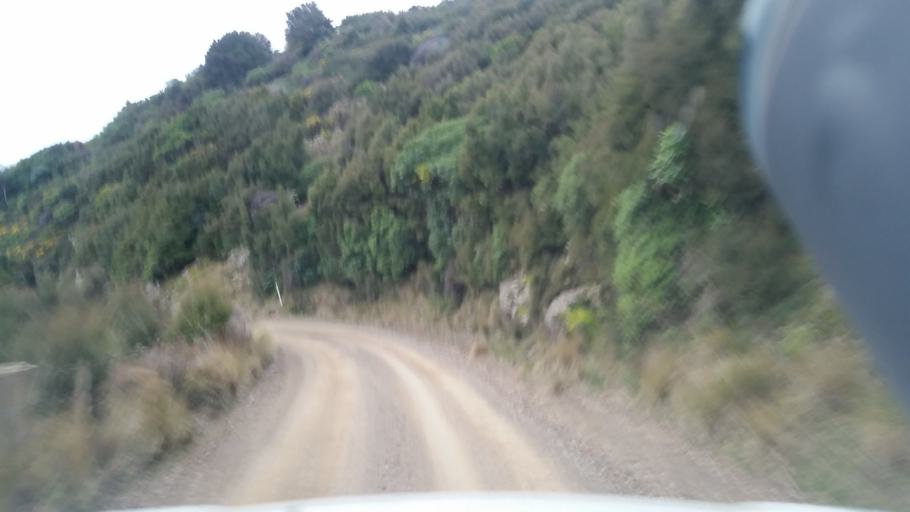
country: NZ
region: Canterbury
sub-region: Christchurch City
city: Christchurch
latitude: -43.8495
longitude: 172.9701
